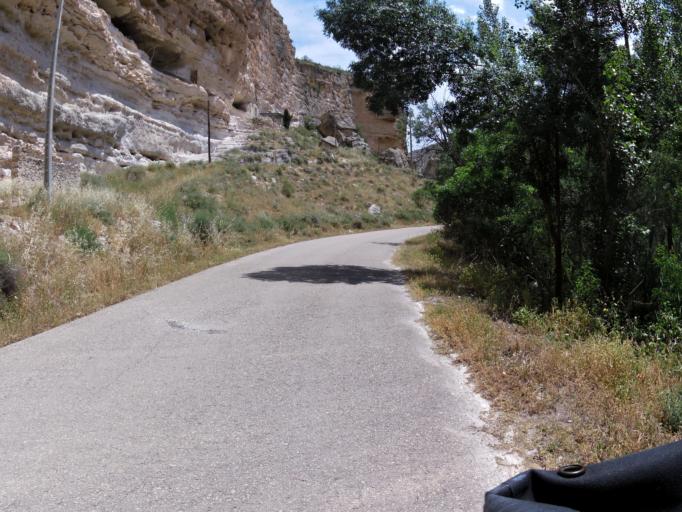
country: ES
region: Castille-La Mancha
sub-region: Provincia de Albacete
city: Casas de Juan Nunez
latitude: 39.1574
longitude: -1.5881
